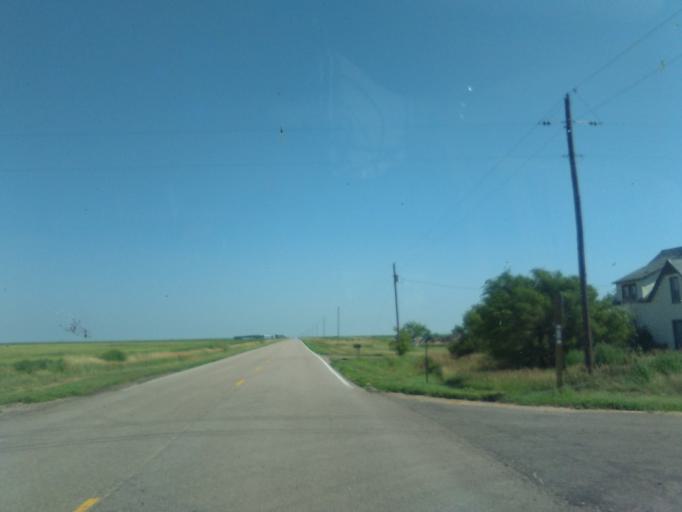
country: US
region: Nebraska
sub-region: Dundy County
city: Benkelman
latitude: 39.8148
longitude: -101.5415
